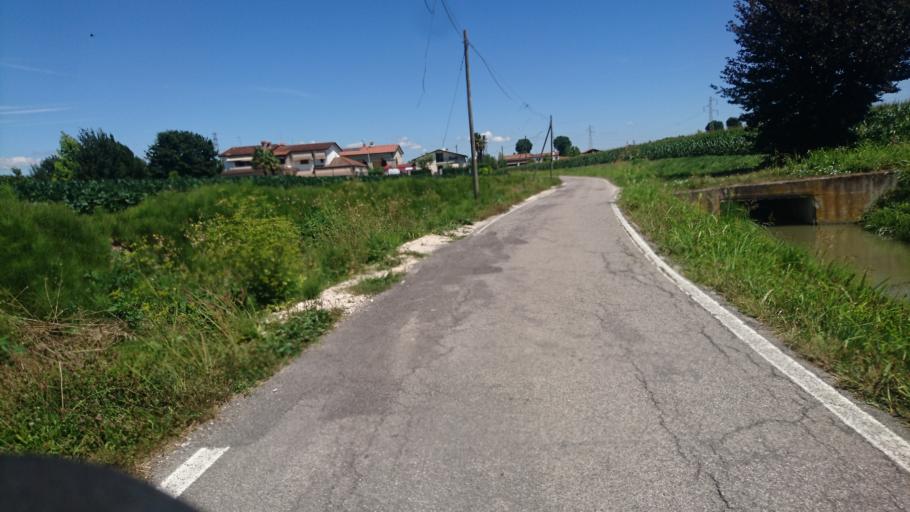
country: IT
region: Veneto
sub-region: Provincia di Padova
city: Sant'Angelo di Piove di Sacco
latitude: 45.2994
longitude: 12.0131
